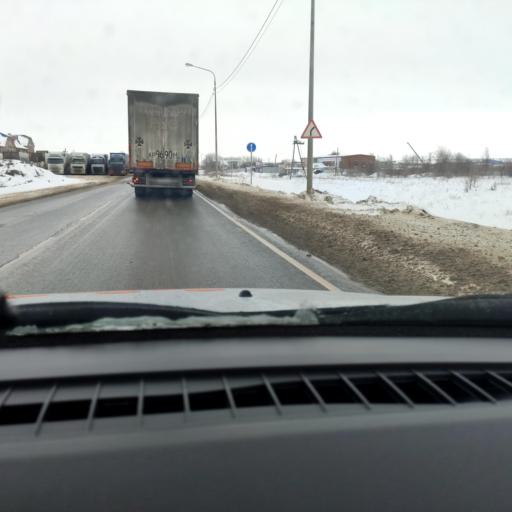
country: RU
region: Samara
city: Dubovyy Umet
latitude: 52.8278
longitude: 50.4978
